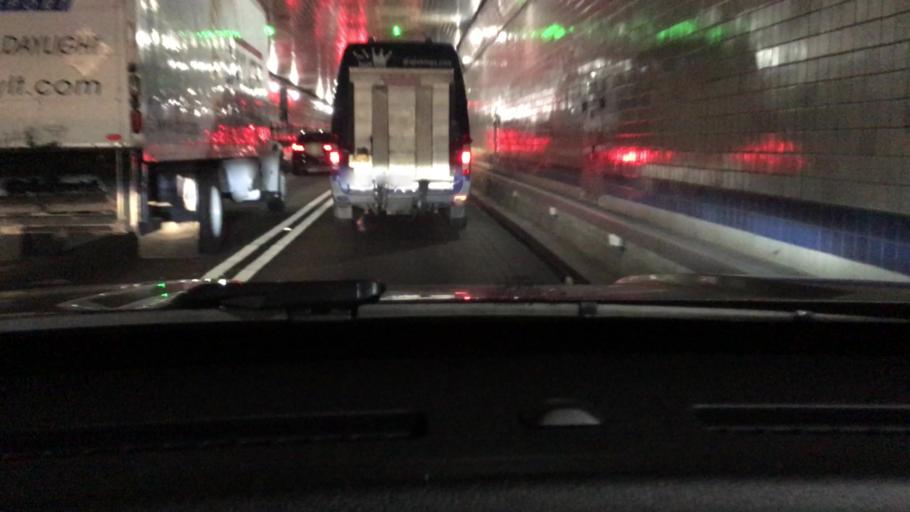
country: US
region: New Jersey
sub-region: Hudson County
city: Weehawken
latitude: 40.7608
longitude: -74.0106
